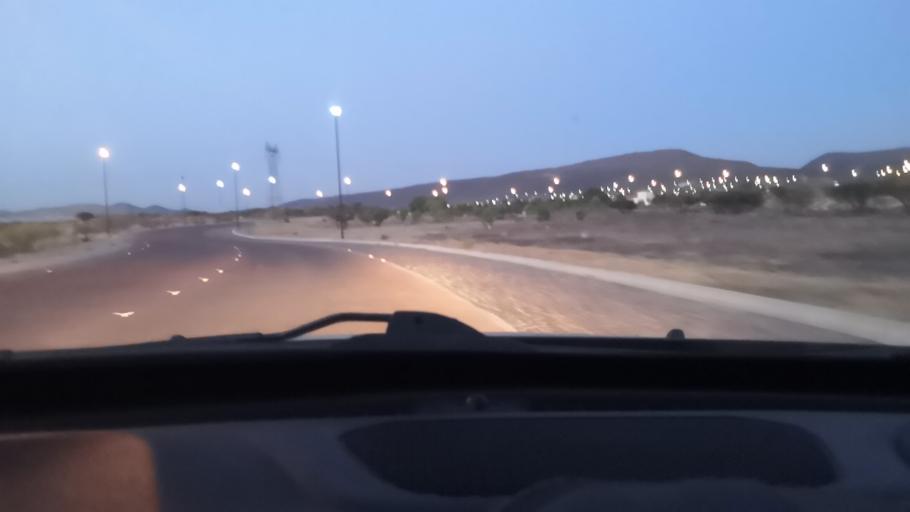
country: MX
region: Guanajuato
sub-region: Leon
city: Fraccionamiento Paseo de las Torres
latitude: 21.2317
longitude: -101.7977
